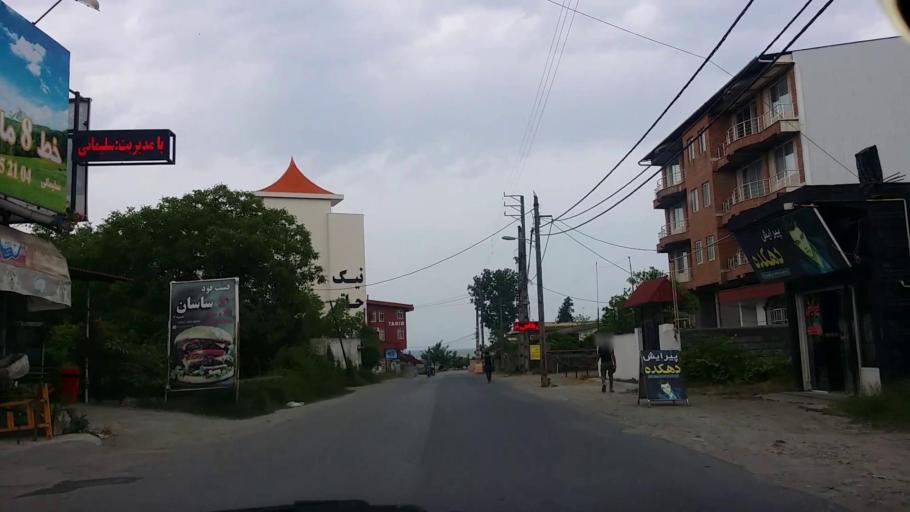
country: IR
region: Mazandaran
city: Chalus
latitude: 36.6852
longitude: 51.4047
